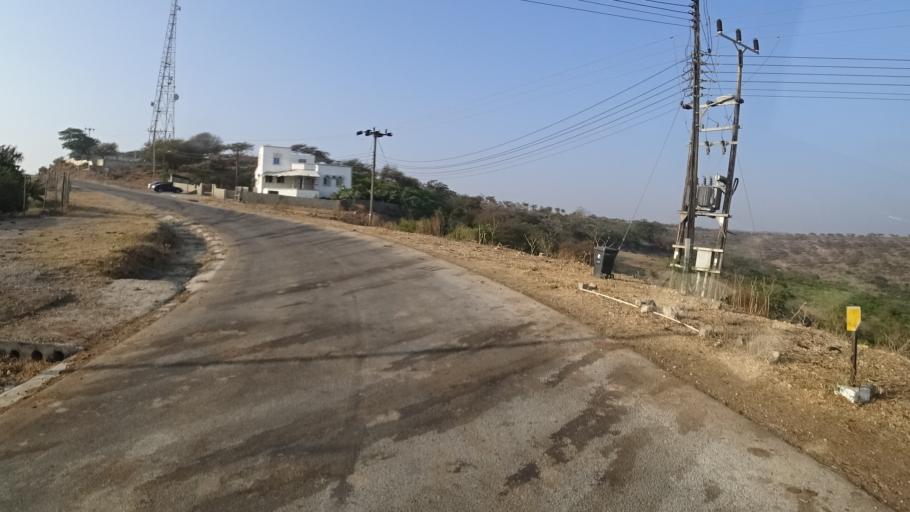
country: YE
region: Al Mahrah
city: Hawf
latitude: 16.7685
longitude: 53.3374
